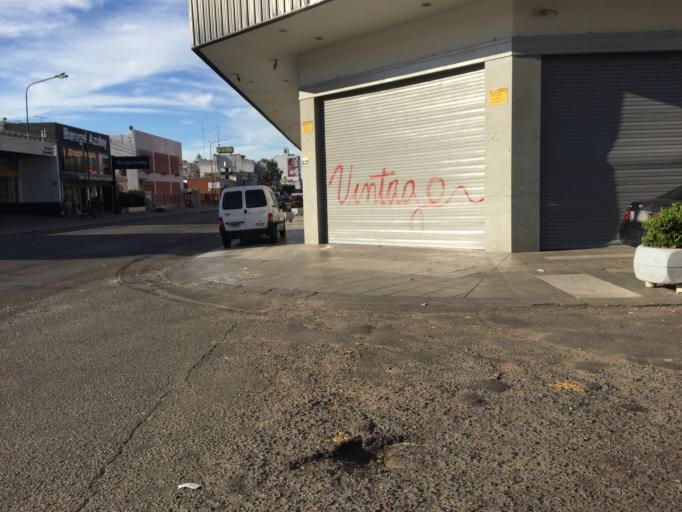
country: AR
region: Buenos Aires
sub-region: Partido de Lomas de Zamora
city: Lomas de Zamora
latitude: -34.7415
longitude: -58.3985
